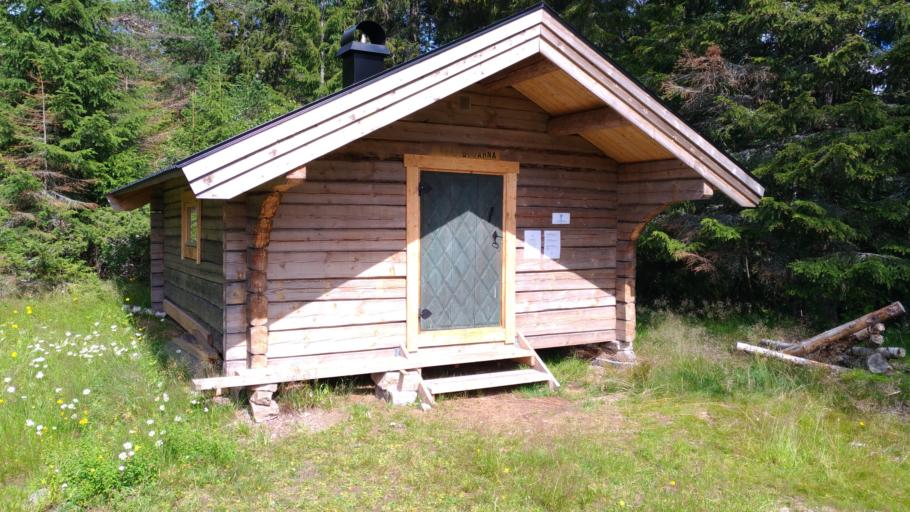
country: SE
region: Dalarna
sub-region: Gagnefs Kommun
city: Mockfjard
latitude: 60.4086
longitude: 15.0712
